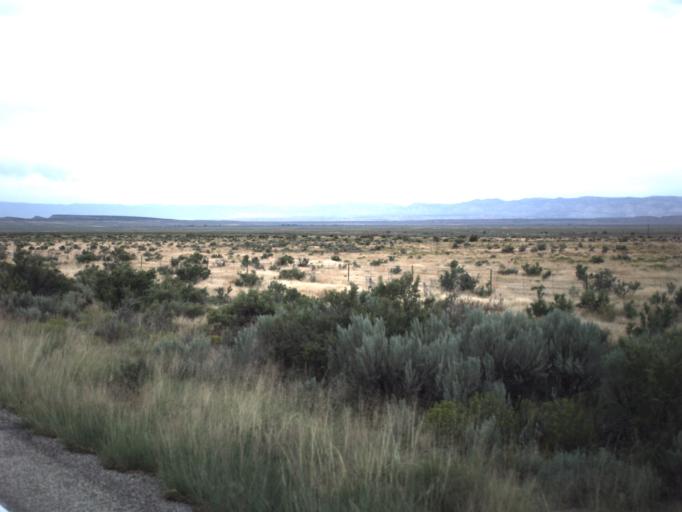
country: US
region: Utah
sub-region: Carbon County
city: East Carbon City
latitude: 39.5354
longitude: -110.5088
